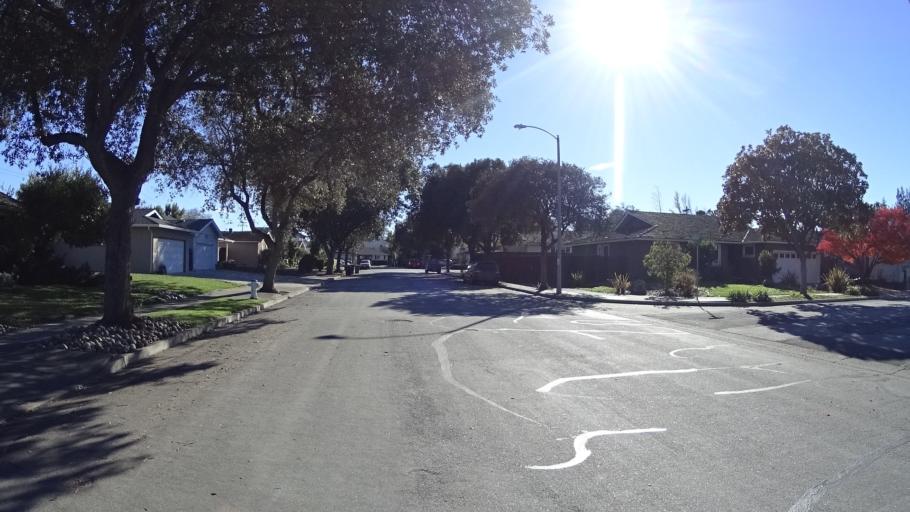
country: US
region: California
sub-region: Santa Clara County
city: Cupertino
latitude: 37.3466
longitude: -122.0238
